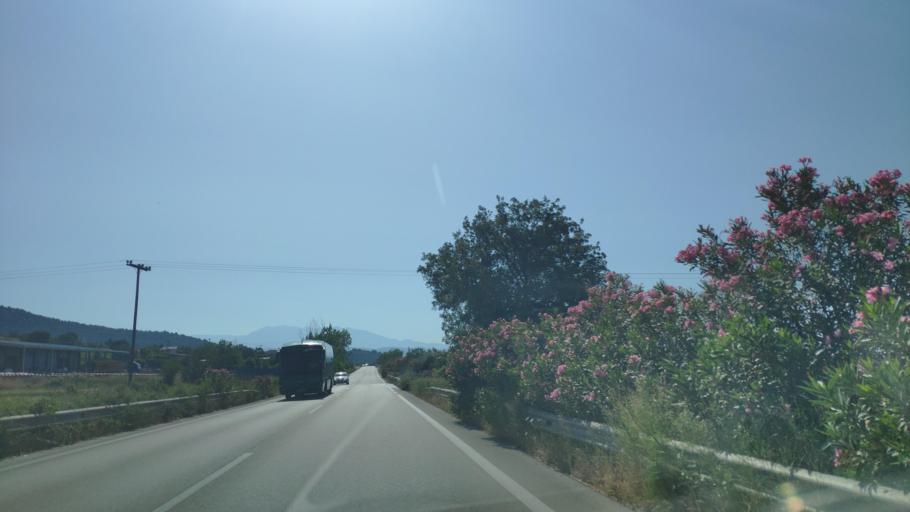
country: GR
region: West Greece
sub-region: Nomos Aitolias kai Akarnanias
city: Lepenou
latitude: 38.6871
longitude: 21.2384
